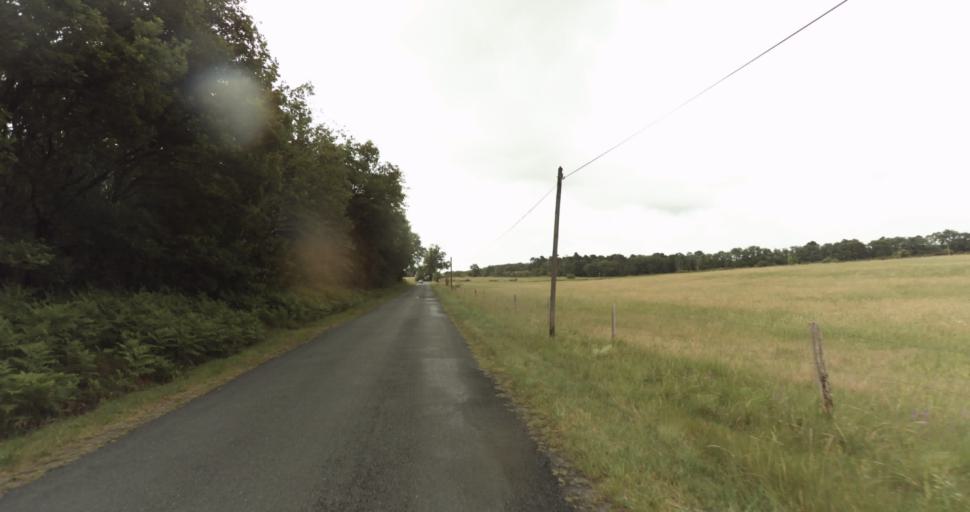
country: FR
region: Aquitaine
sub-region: Departement de la Dordogne
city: Belves
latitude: 44.7516
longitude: 0.9691
